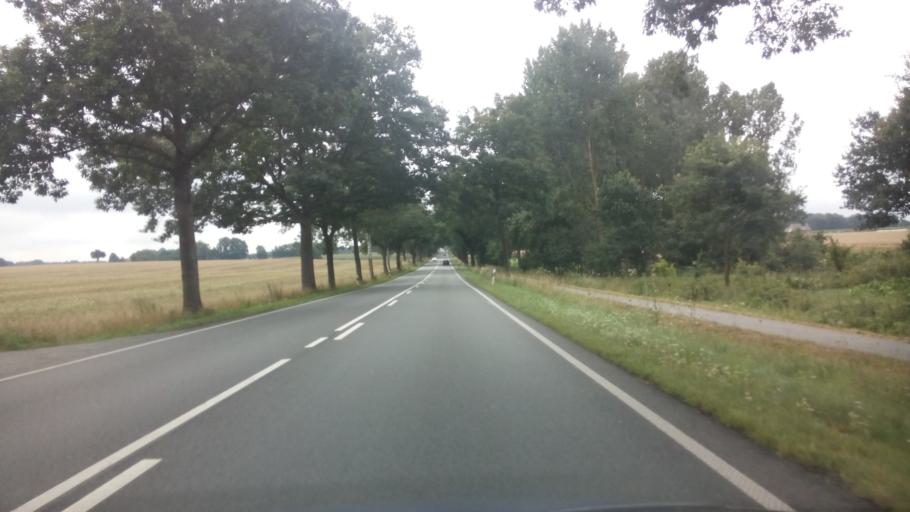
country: DE
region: Lower Saxony
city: Bassum
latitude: 52.8820
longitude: 8.7290
